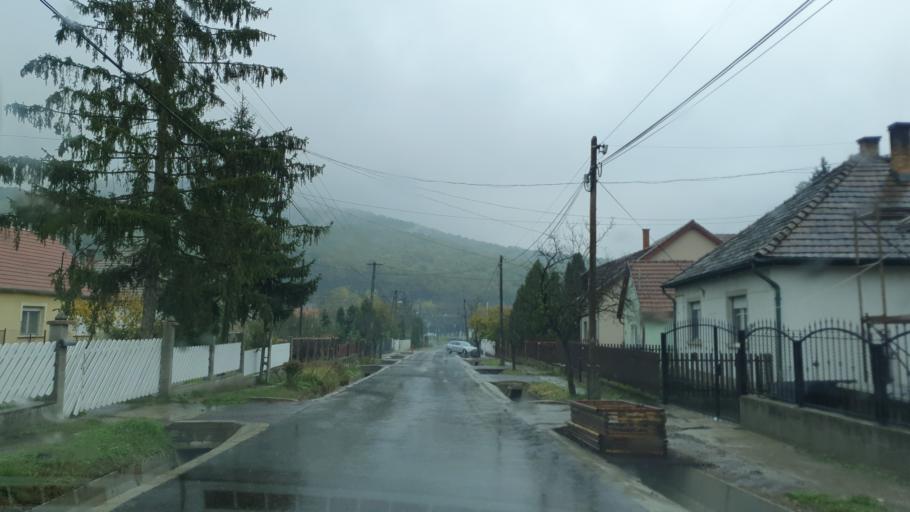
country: HU
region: Pest
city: Veroce
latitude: 47.8455
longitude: 19.0958
